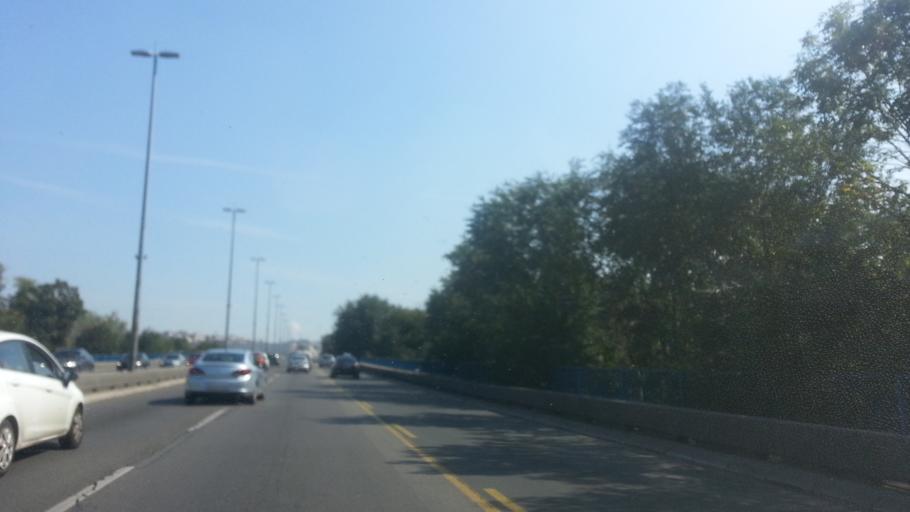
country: RS
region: Central Serbia
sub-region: Belgrade
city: Novi Beograd
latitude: 44.8145
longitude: 20.4416
